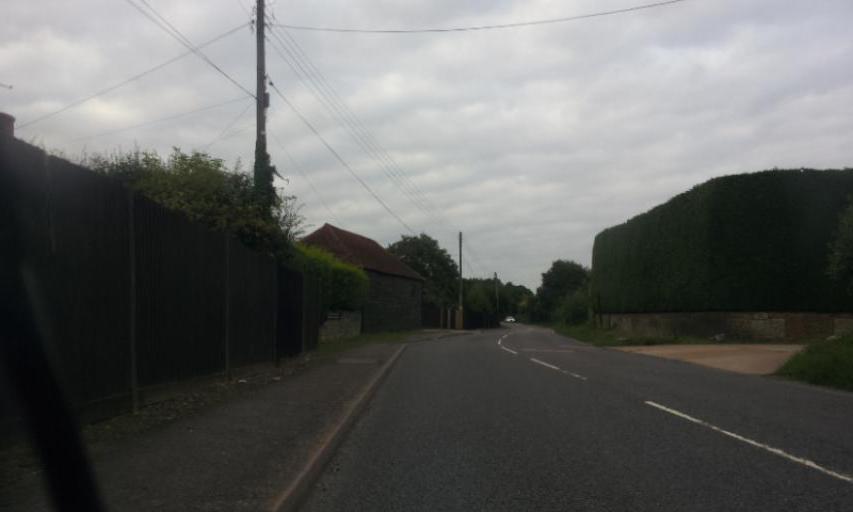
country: GB
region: England
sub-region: Kent
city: Yalding
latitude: 51.2343
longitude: 0.4084
